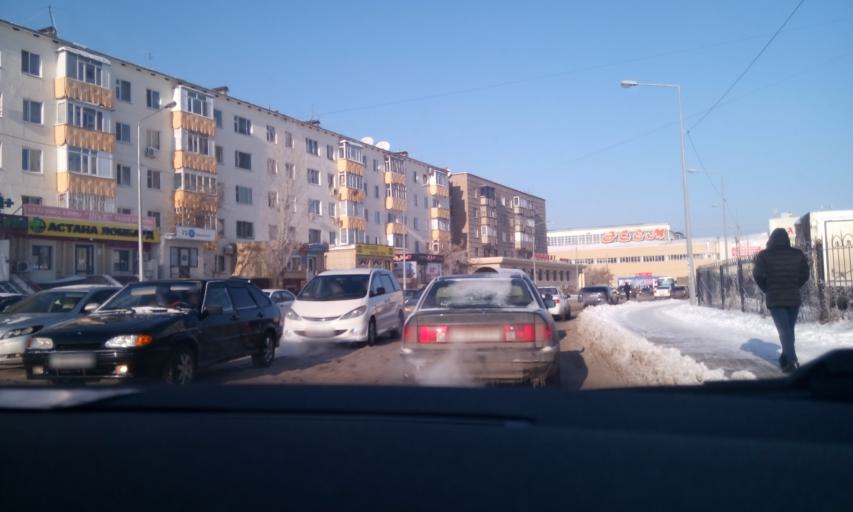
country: KZ
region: Astana Qalasy
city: Astana
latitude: 51.1795
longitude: 71.4360
